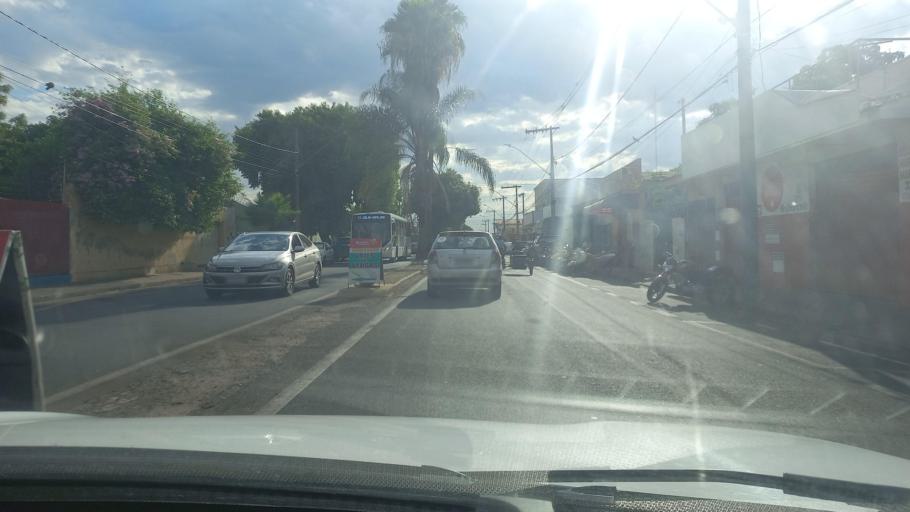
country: BR
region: Minas Gerais
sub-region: Uberaba
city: Uberaba
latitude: -19.7694
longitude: -47.9285
